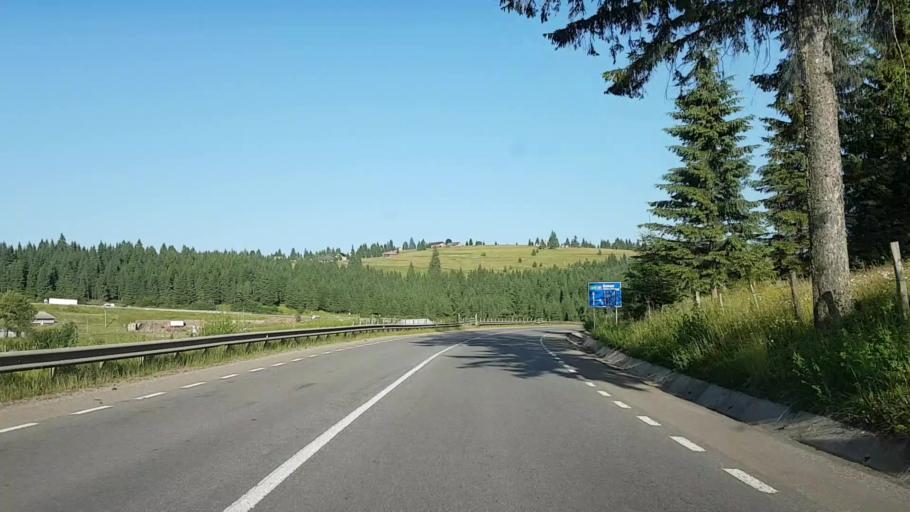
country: RO
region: Bistrita-Nasaud
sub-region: Comuna Lunca Ilvei
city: Lunca Ilvei
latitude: 47.2418
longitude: 25.0127
